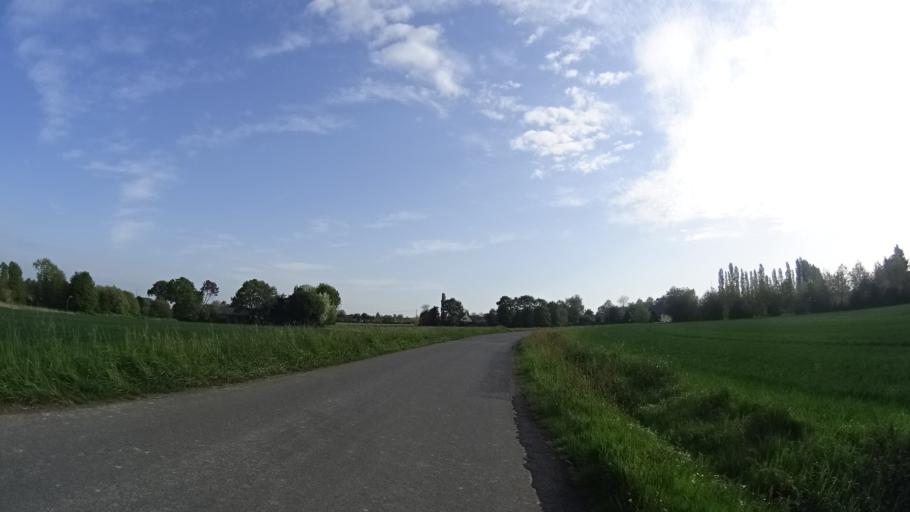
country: FR
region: Brittany
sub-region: Departement d'Ille-et-Vilaine
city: La Meziere
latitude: 48.2157
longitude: -1.7633
